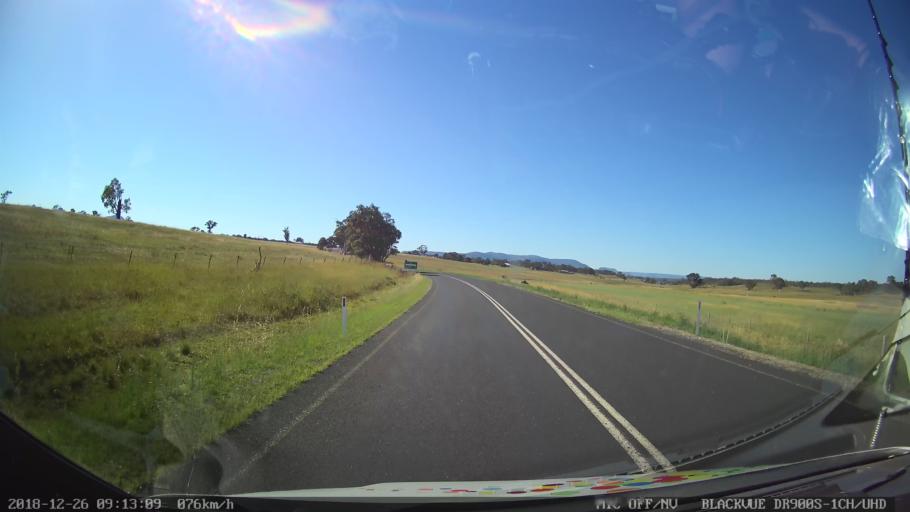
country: AU
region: New South Wales
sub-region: Mid-Western Regional
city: Kandos
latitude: -32.7649
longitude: 149.9777
